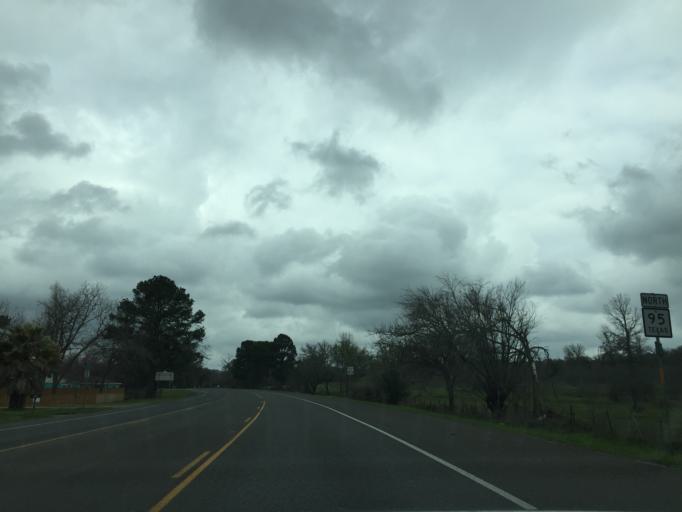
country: US
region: Texas
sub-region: Bastrop County
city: Bastrop
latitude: 30.1176
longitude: -97.3080
